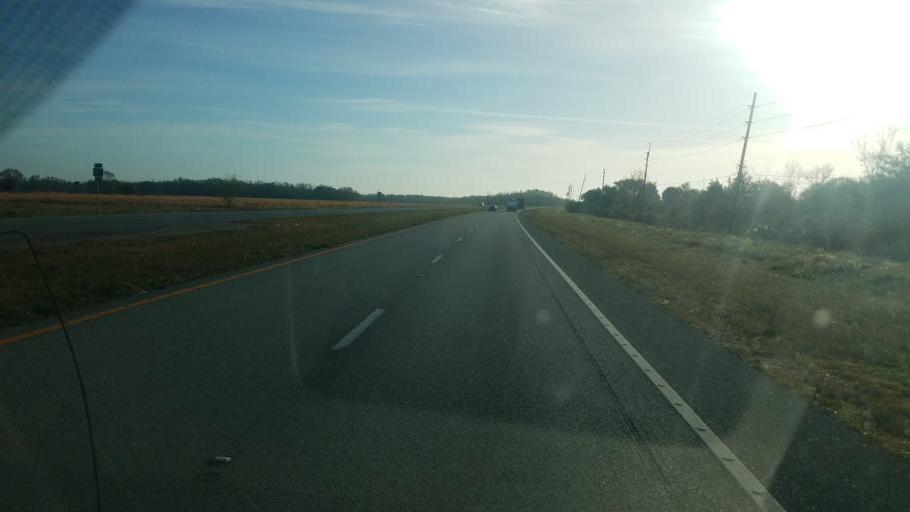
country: US
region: Florida
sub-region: Osceola County
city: Saint Cloud
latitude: 28.1448
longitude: -81.0745
